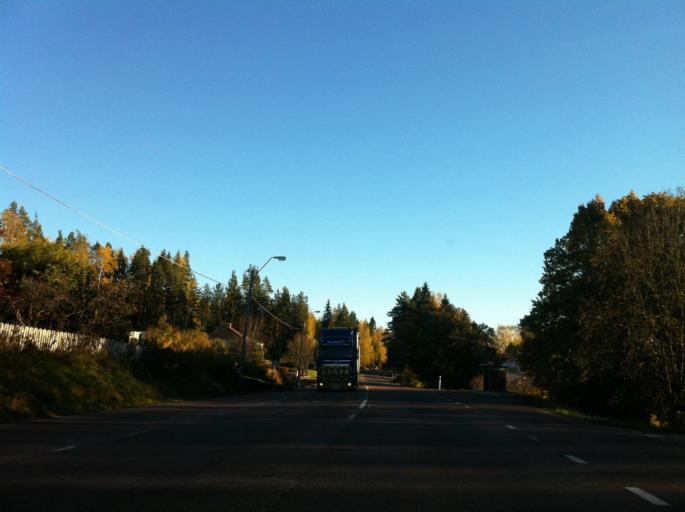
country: SE
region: Dalarna
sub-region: Faluns Kommun
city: Grycksbo
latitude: 60.6969
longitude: 15.4815
